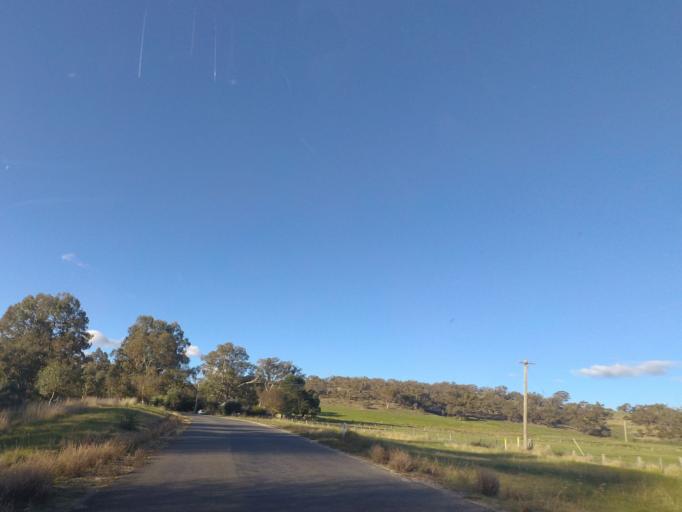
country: AU
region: Victoria
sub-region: Mount Alexander
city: Castlemaine
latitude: -37.1473
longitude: 144.1848
